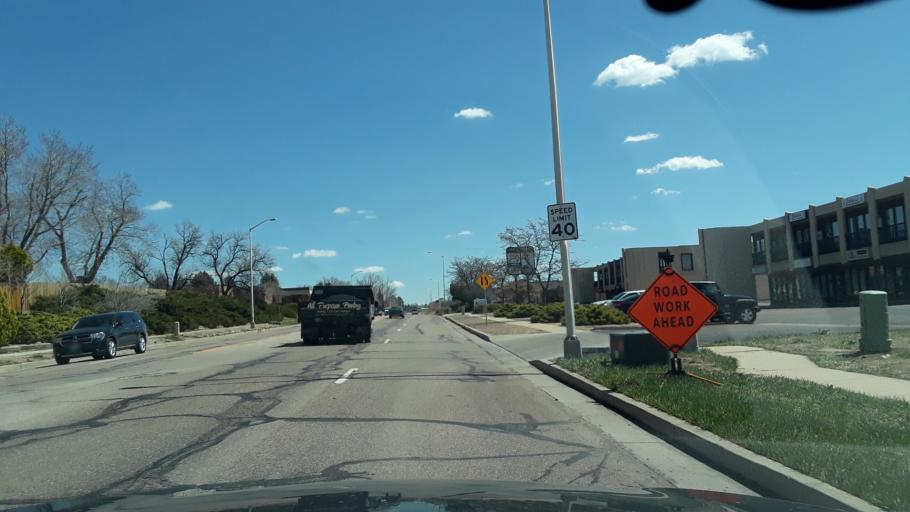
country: US
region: Colorado
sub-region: El Paso County
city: Cimarron Hills
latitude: 38.8467
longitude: -104.7320
